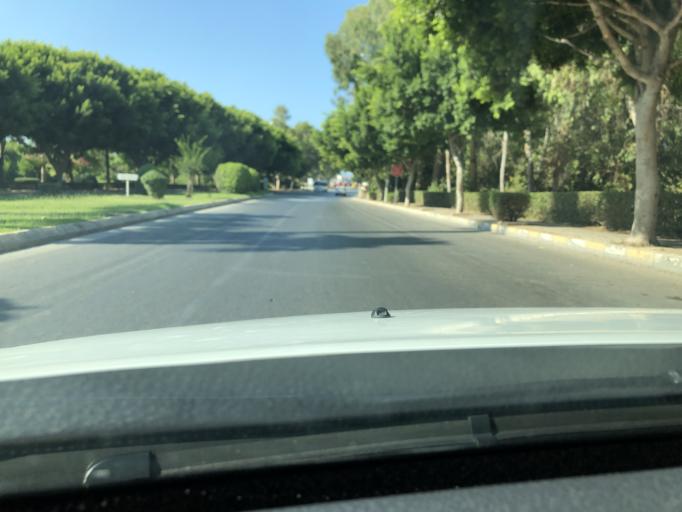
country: TR
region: Antalya
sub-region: Manavgat
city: Side
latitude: 36.7755
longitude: 31.3963
